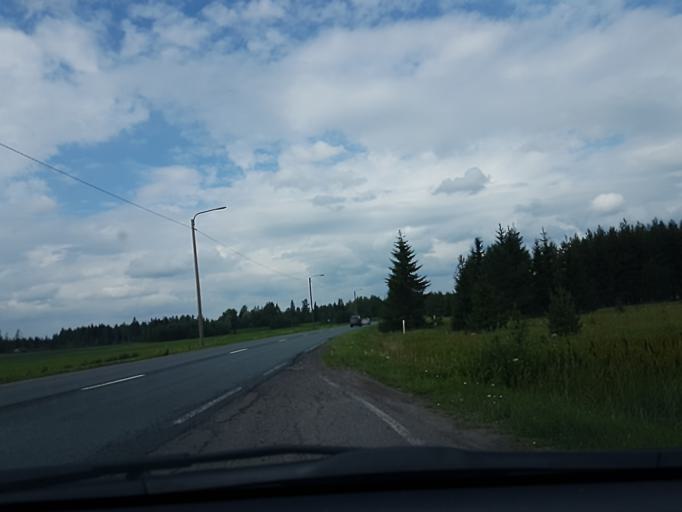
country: FI
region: Uusimaa
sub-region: Helsinki
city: Jaervenpaeae
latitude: 60.5172
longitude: 25.1000
